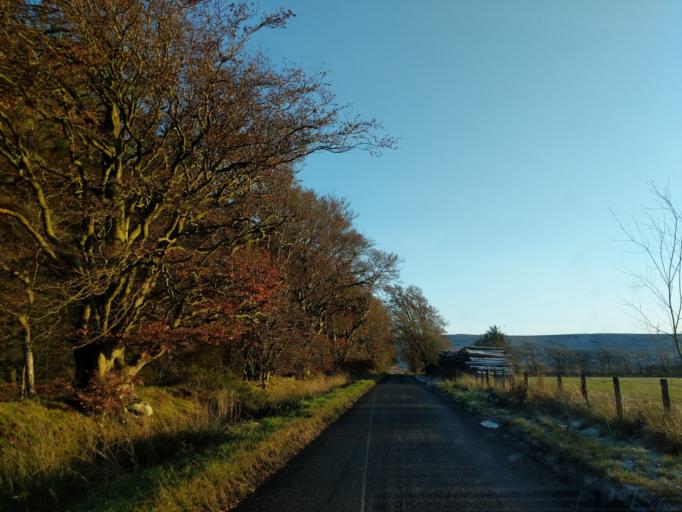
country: GB
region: Scotland
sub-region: Edinburgh
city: Balerno
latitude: 55.8567
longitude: -3.3624
